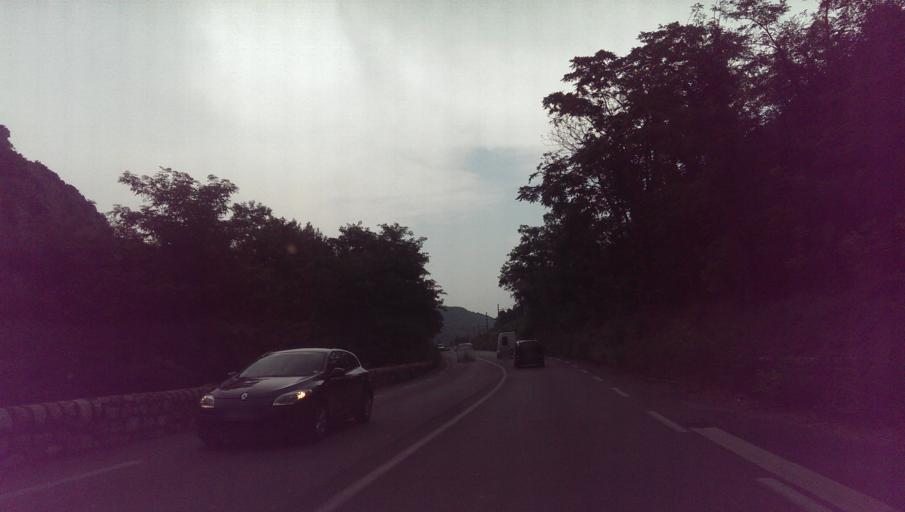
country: FR
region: Languedoc-Roussillon
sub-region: Departement des Pyrenees-Orientales
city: Ria-Sirach
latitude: 42.5968
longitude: 2.3769
